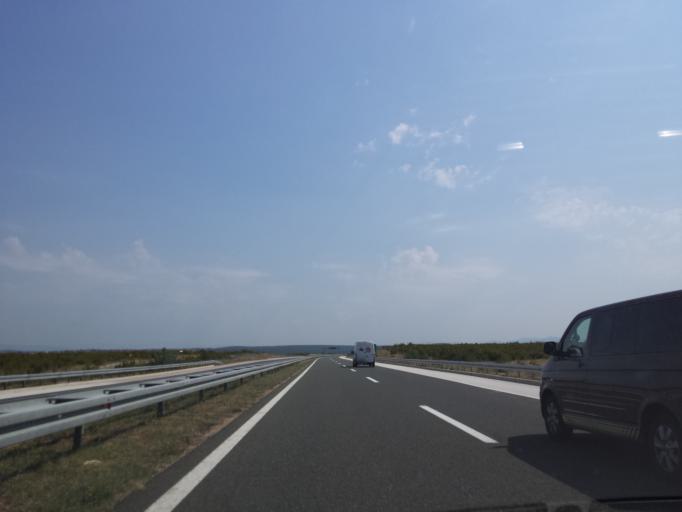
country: HR
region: Sibensko-Kniniska
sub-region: Grad Sibenik
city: Pirovac
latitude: 43.9033
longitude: 15.7682
